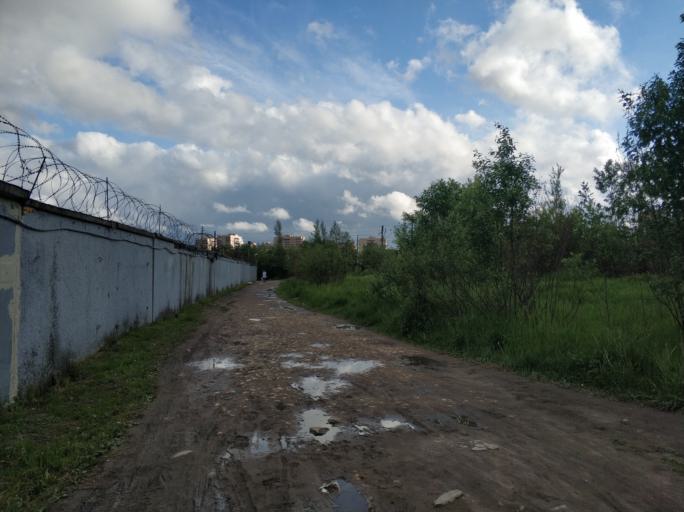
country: RU
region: Leningrad
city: Murino
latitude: 60.0444
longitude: 30.4298
